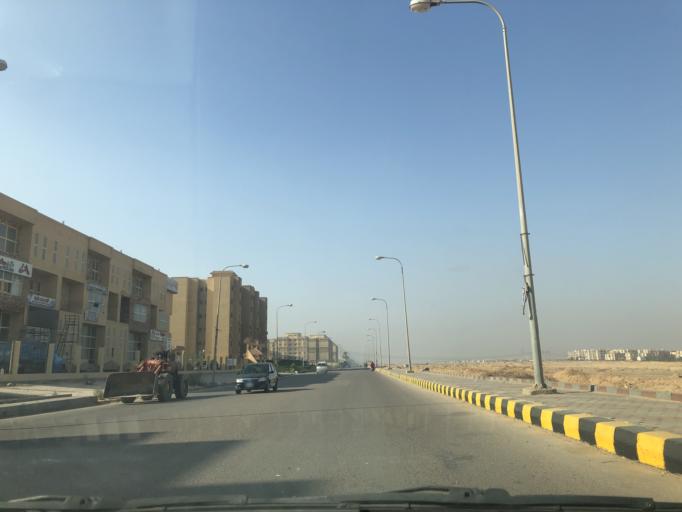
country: EG
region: Al Jizah
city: Madinat Sittah Uktubar
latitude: 29.9172
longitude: 31.0601
